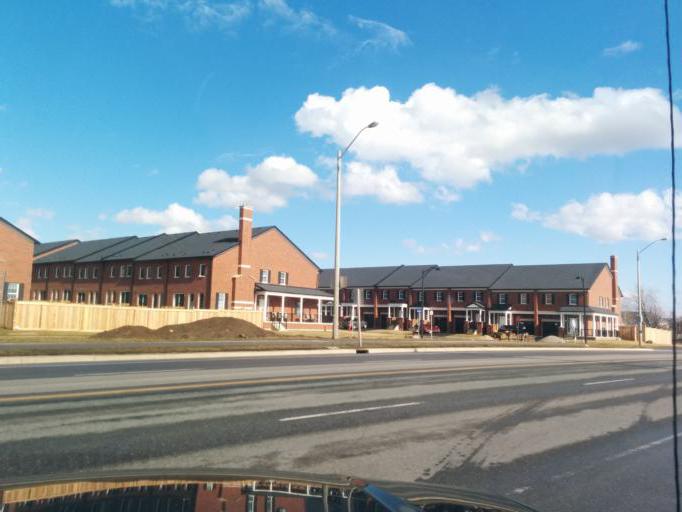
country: CA
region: Ontario
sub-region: Halton
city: Milton
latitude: 43.4936
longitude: -79.8683
